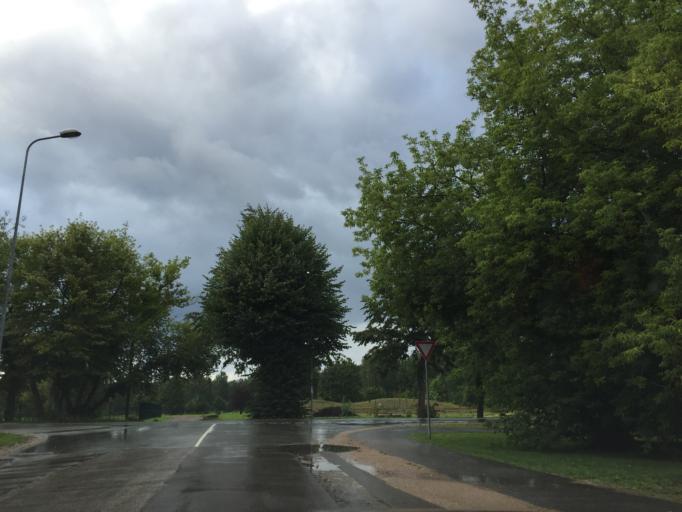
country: LV
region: Babite
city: Pinki
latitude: 56.9566
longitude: 23.9476
